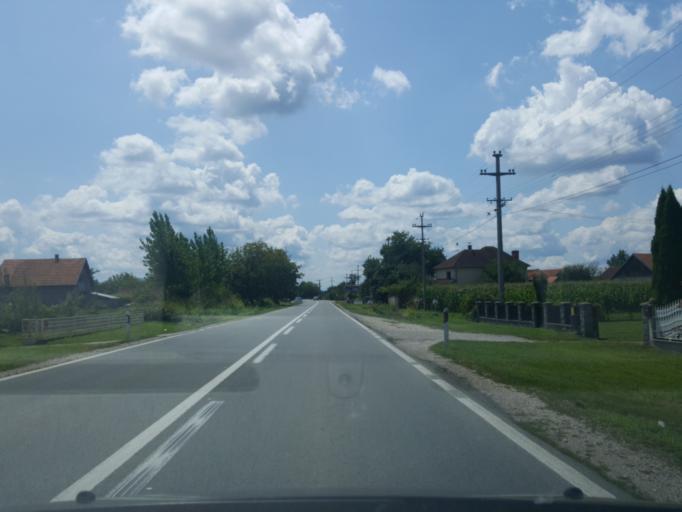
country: RS
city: Lesnica
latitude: 44.6372
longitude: 19.2768
